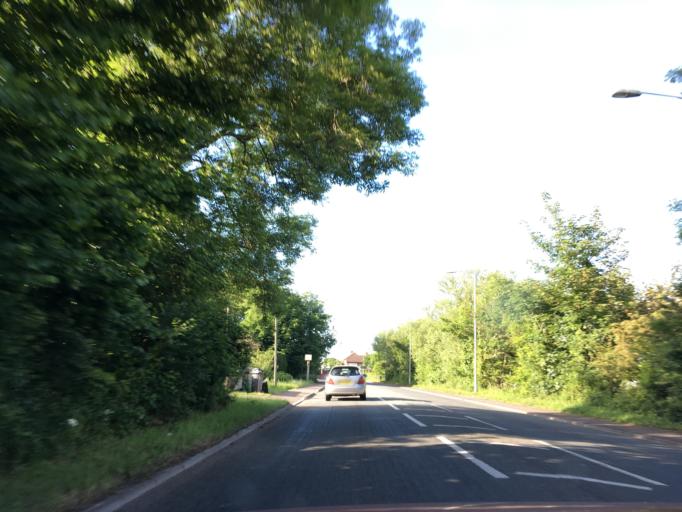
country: GB
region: England
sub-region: Somerset
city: Highbridge
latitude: 51.2016
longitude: -2.9899
